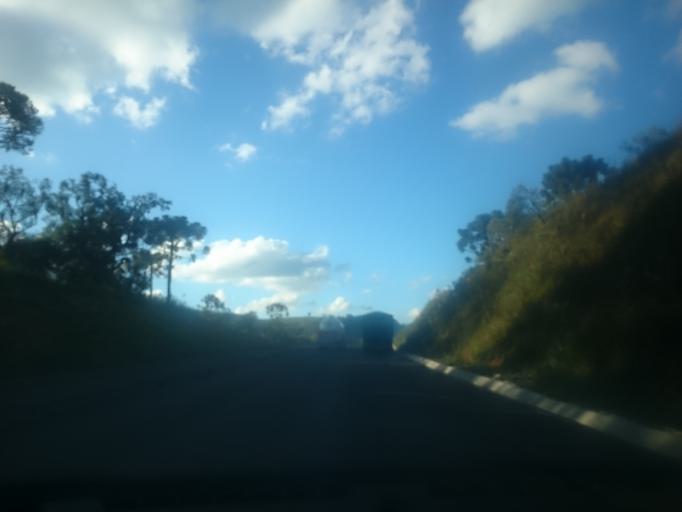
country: BR
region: Santa Catarina
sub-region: Sao Joaquim
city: Sao Joaquim
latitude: -28.0756
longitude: -50.0721
